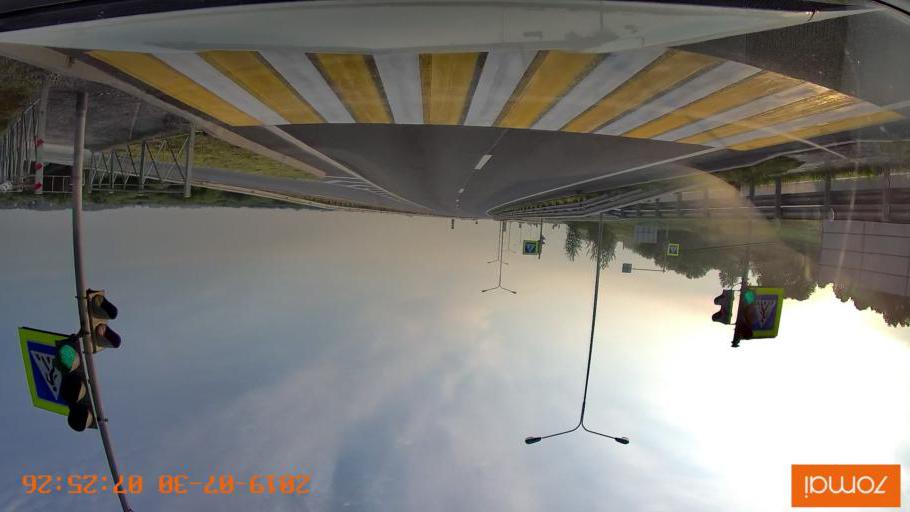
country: RU
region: Kaliningrad
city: Gvardeysk
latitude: 54.6868
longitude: 20.8352
